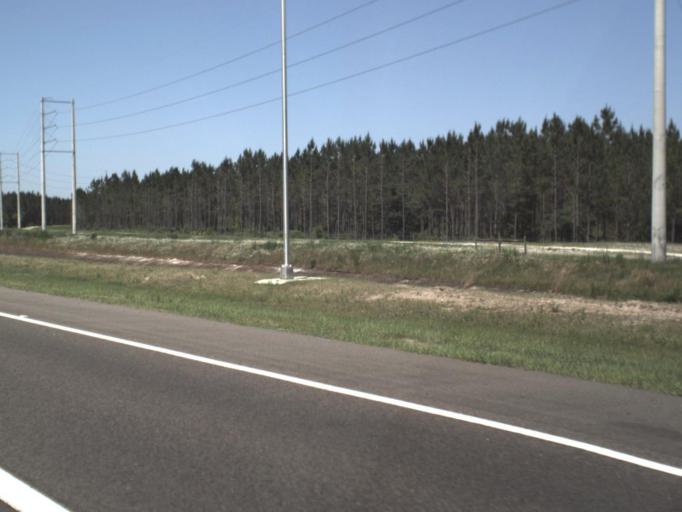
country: US
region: Florida
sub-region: Duval County
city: Baldwin
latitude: 30.2975
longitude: -81.8783
